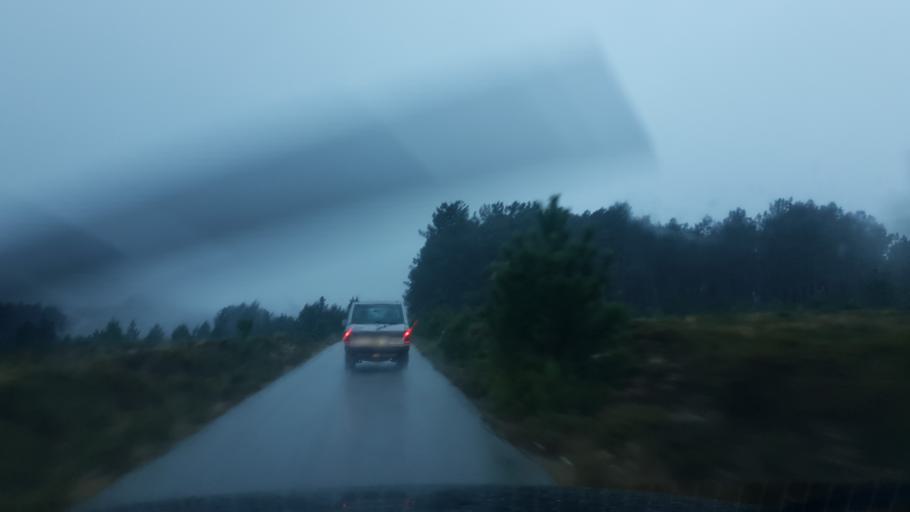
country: PT
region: Viseu
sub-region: Sao Pedro do Sul
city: Sao Pedro do Sul
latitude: 40.8298
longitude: -8.1340
